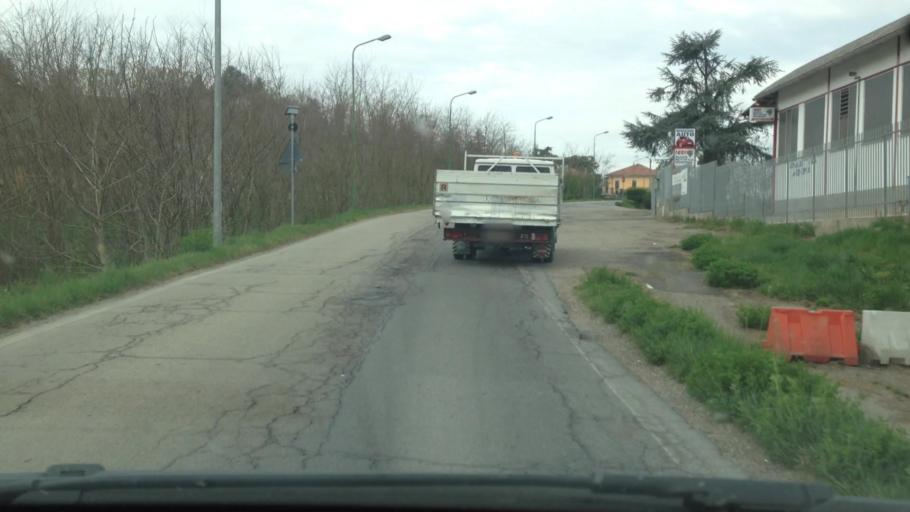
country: IT
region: Piedmont
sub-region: Provincia di Asti
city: Asti
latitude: 44.8952
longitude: 8.1870
